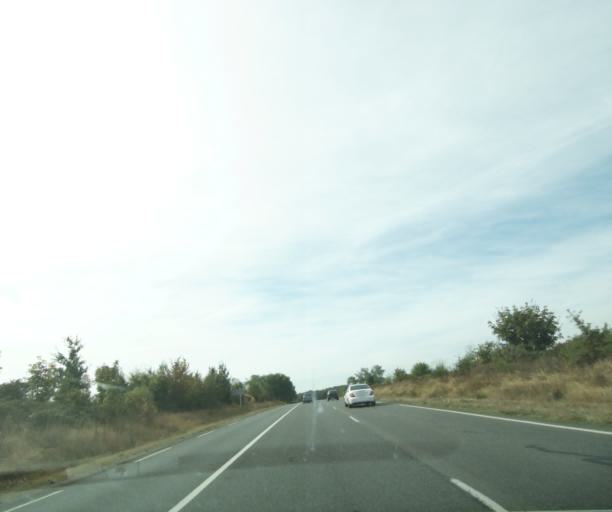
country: FR
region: Auvergne
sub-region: Departement de l'Allier
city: Lapalisse
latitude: 46.2419
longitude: 3.6109
